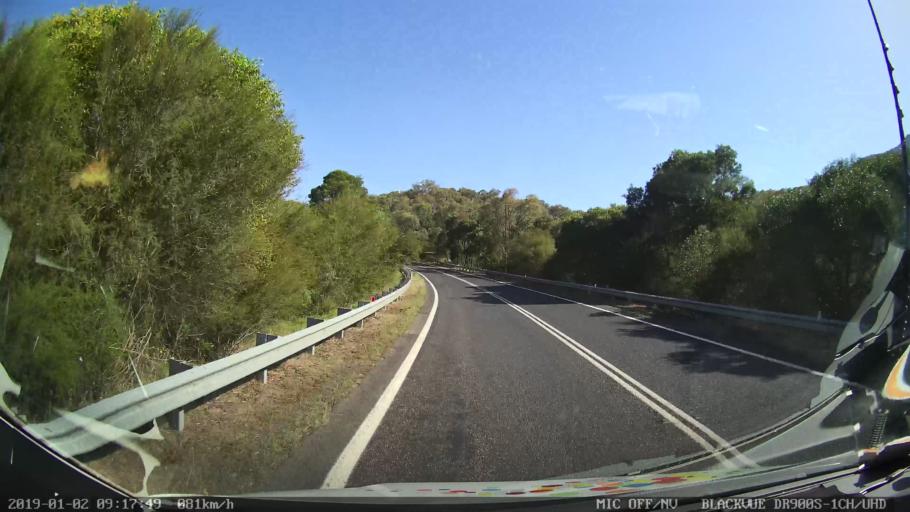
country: AU
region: New South Wales
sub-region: Tumut Shire
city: Tumut
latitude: -35.4355
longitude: 148.2874
